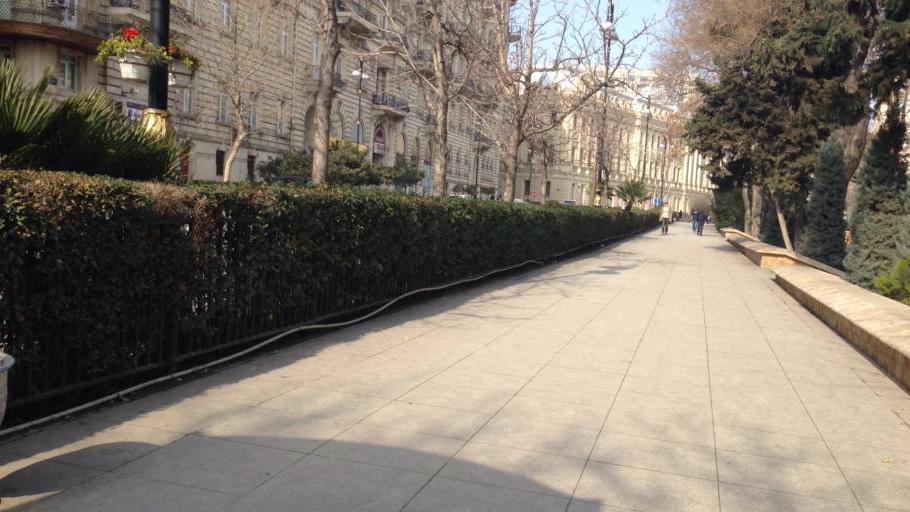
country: AZ
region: Baki
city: Badamdar
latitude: 40.3649
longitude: 49.8312
